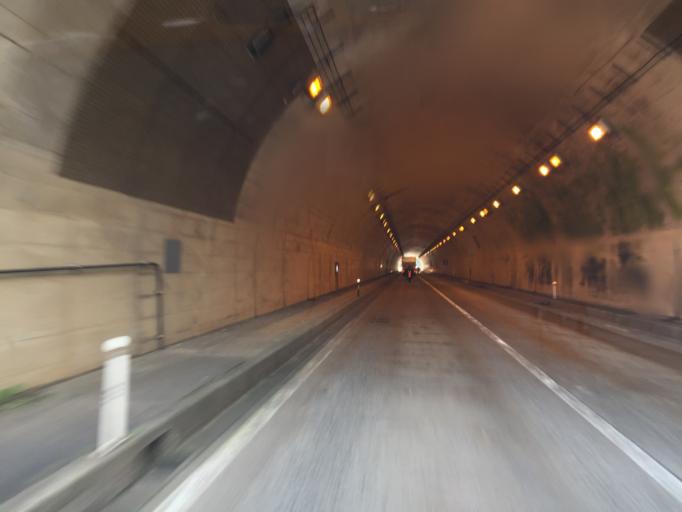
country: JP
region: Fukushima
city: Kitakata
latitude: 37.7739
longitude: 139.9204
